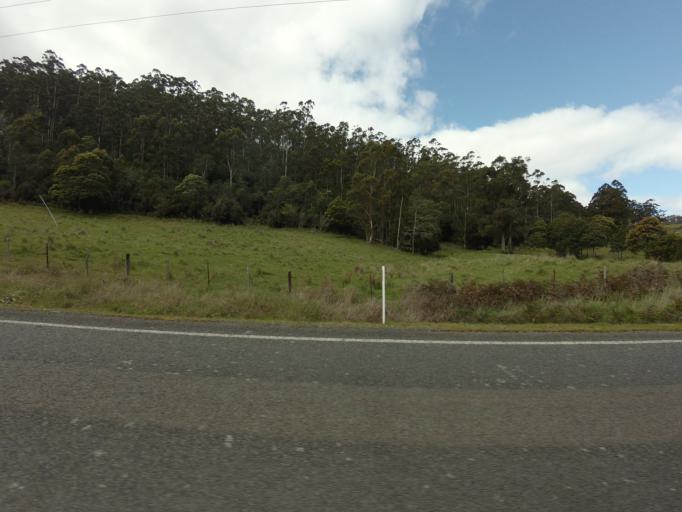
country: AU
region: Tasmania
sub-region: Huon Valley
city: Cygnet
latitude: -43.2816
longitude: 147.0107
